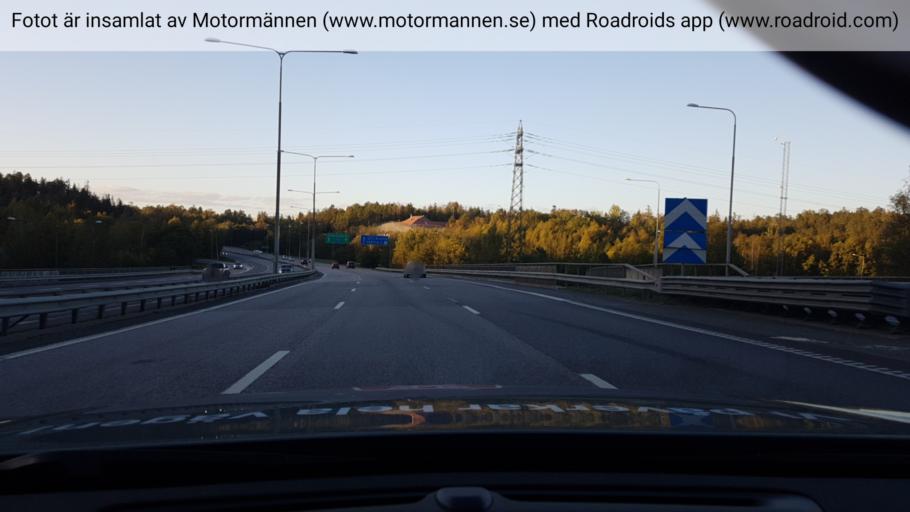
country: SE
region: Stockholm
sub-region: Haninge Kommun
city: Handen
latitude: 59.2173
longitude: 18.1352
